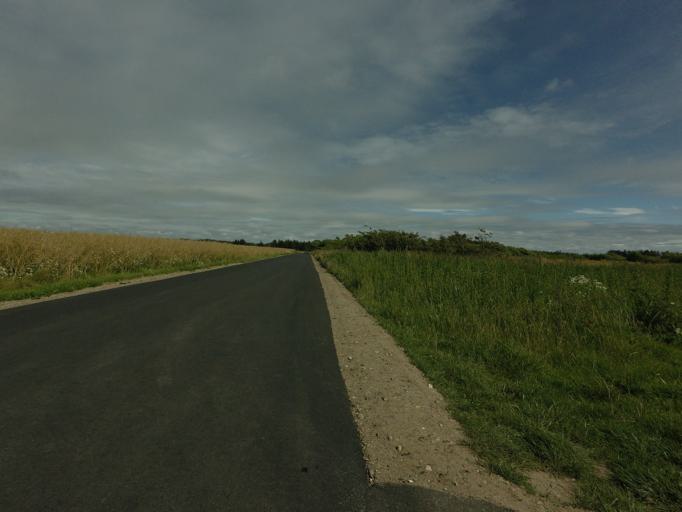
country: DK
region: North Denmark
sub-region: Hjorring Kommune
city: Vra
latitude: 57.3957
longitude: 9.7683
